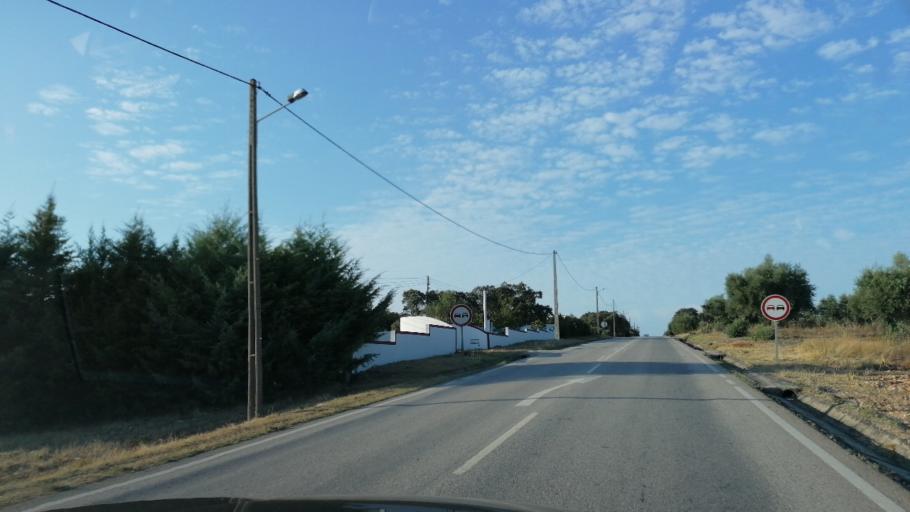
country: PT
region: Santarem
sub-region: Alcanena
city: Alcanena
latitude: 39.4425
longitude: -8.6244
